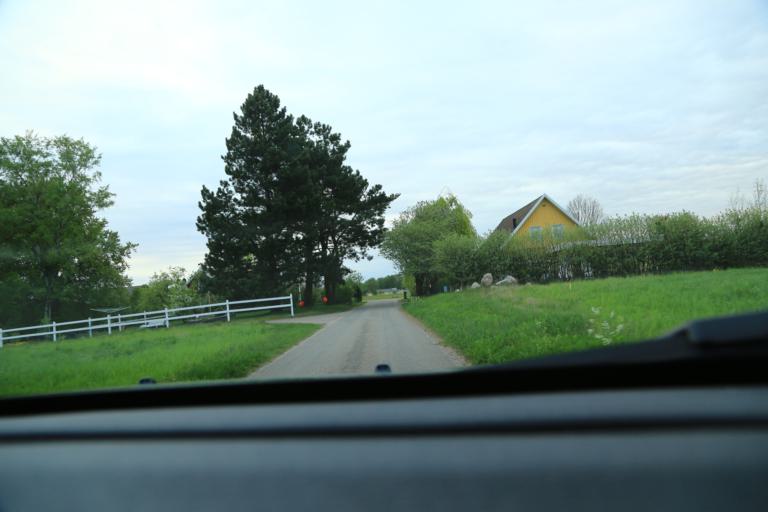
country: SE
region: Halland
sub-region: Varbergs Kommun
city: Varberg
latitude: 57.1512
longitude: 12.2384
